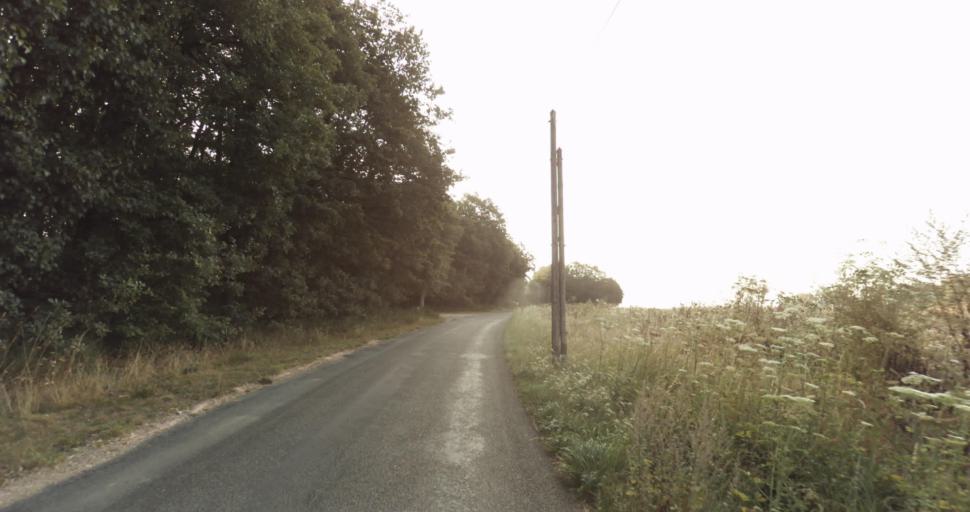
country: FR
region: Centre
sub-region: Departement d'Eure-et-Loir
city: Vert-en-Drouais
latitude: 48.7790
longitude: 1.3214
